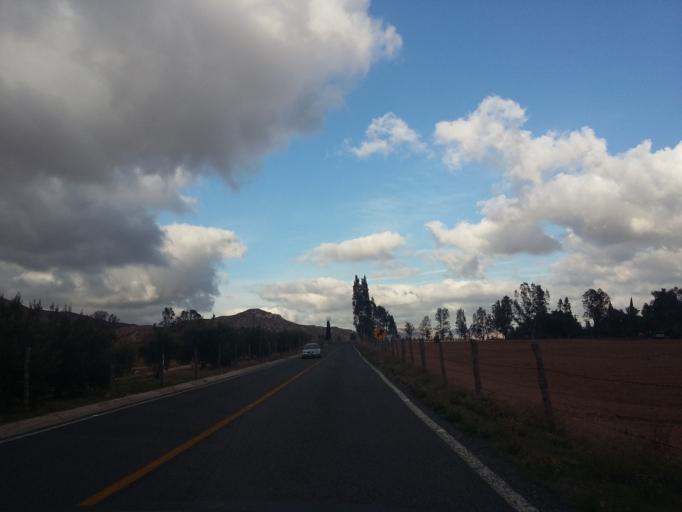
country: MX
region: Baja California
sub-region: Ensenada
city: Rancho Verde
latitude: 32.0463
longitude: -116.6672
